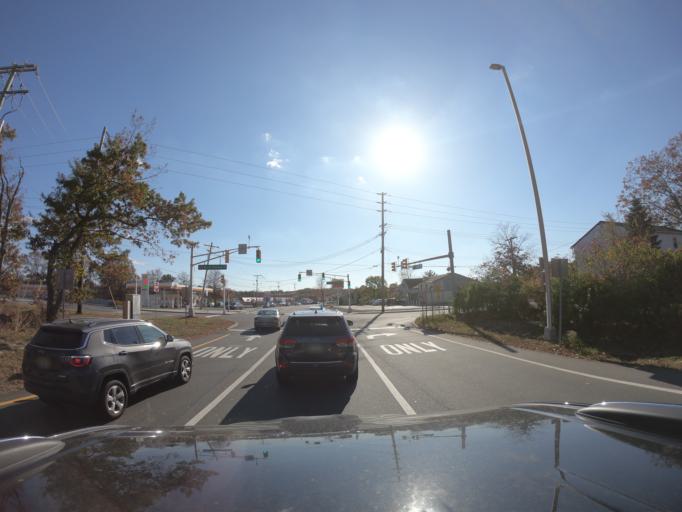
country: US
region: New Jersey
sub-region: Monmouth County
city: Ramtown
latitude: 40.0980
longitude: -74.1443
